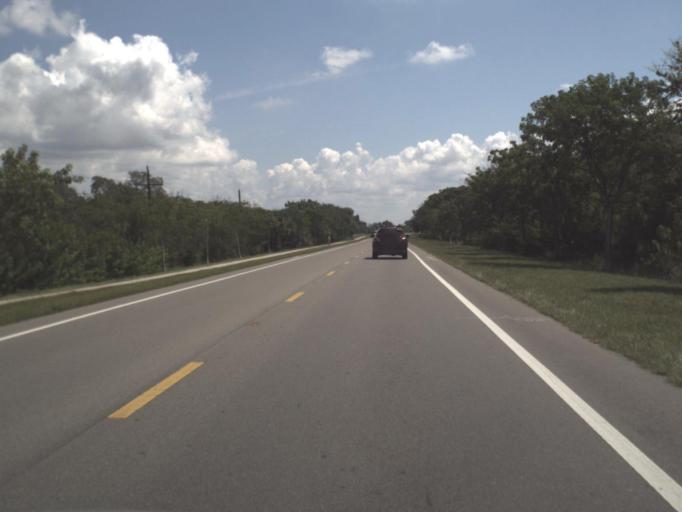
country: US
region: Florida
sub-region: Manatee County
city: Cortez
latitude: 27.4963
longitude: -82.6817
